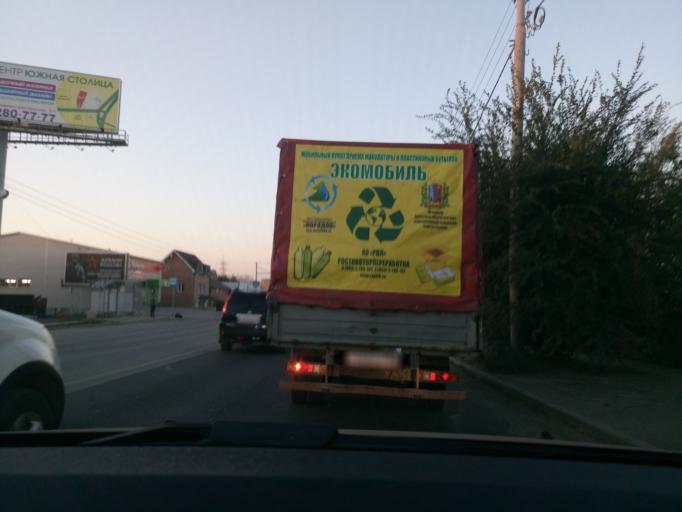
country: RU
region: Rostov
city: Kalinin
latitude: 47.2509
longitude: 39.6142
